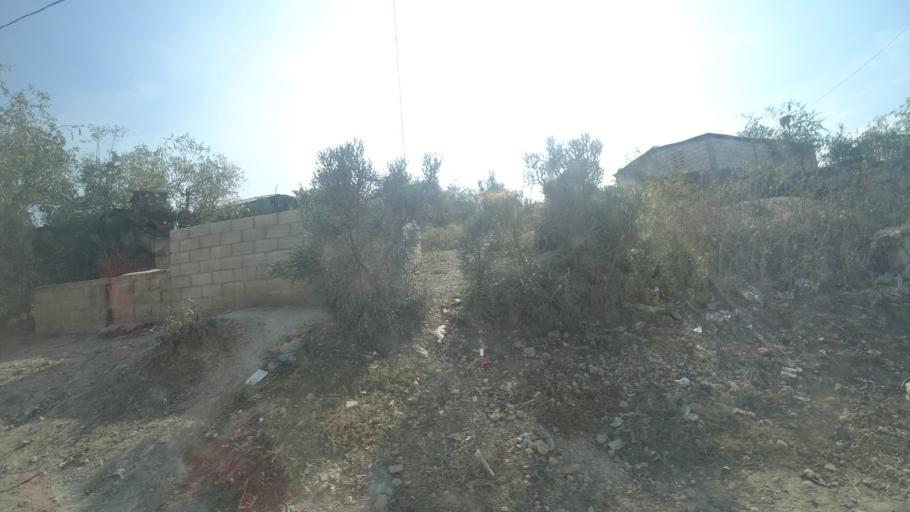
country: HT
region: Ouest
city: Croix des Bouquets
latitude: 18.6575
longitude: -72.2865
